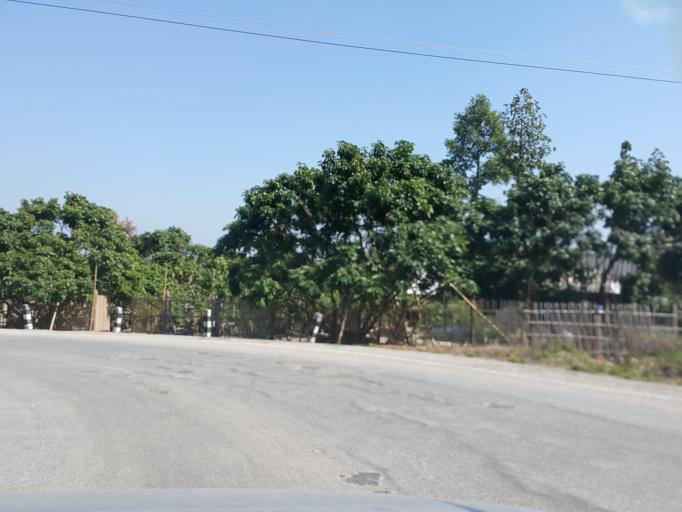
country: TH
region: Chiang Mai
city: Doi Lo
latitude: 18.5266
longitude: 98.7602
